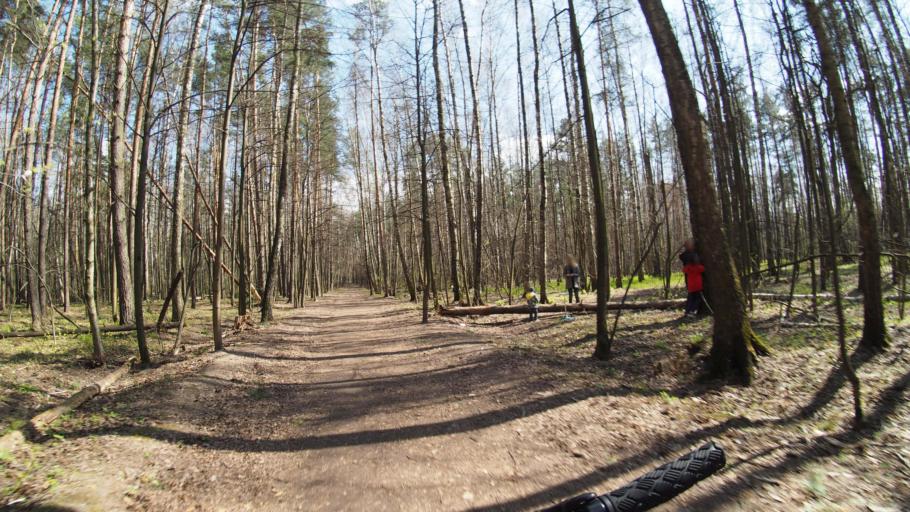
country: RU
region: Moskovskaya
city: Ramenskoye
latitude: 55.5806
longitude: 38.2292
